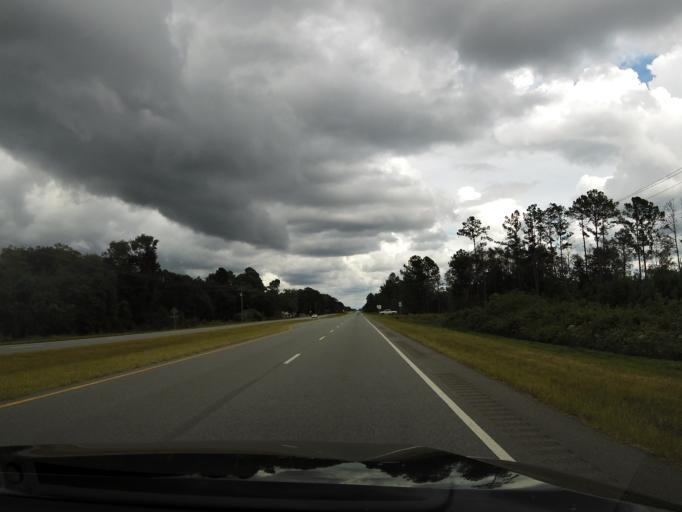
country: US
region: Georgia
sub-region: Brantley County
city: Nahunta
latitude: 31.2142
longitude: -81.9039
